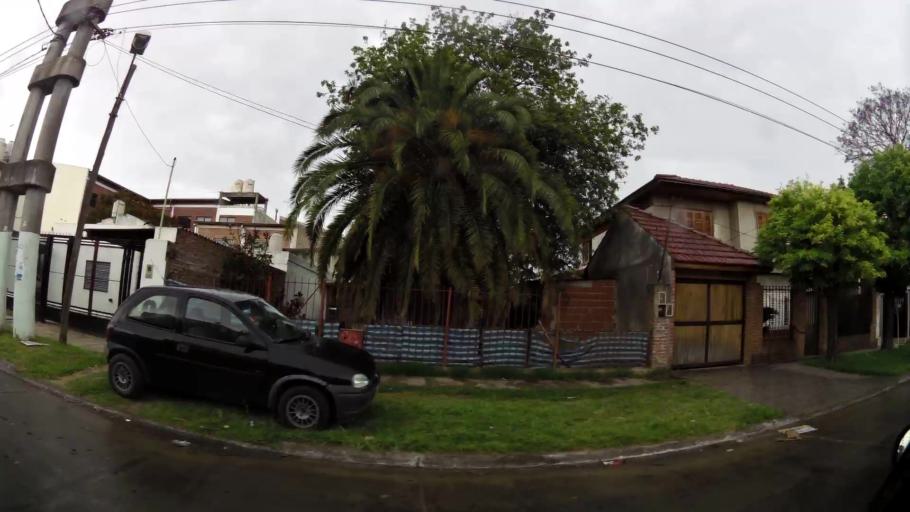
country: AR
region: Buenos Aires
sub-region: Partido de Quilmes
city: Quilmes
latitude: -34.7713
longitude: -58.2171
